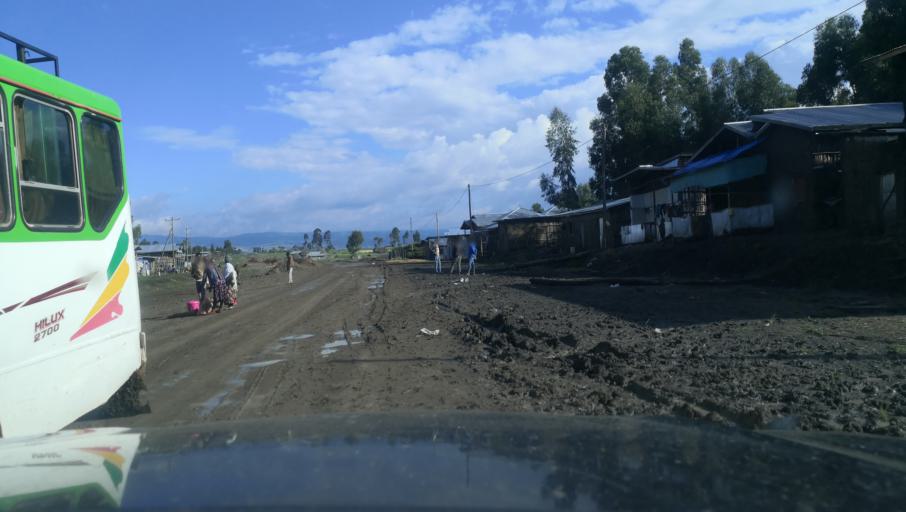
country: ET
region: Oromiya
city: Tulu Bolo
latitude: 8.5415
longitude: 38.2516
